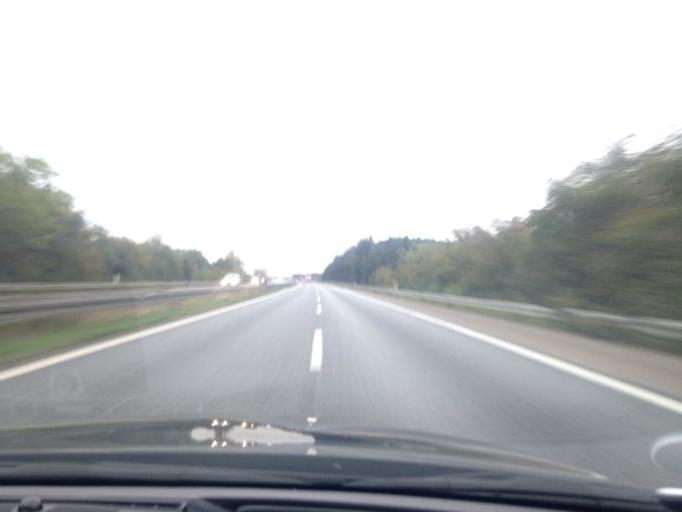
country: DK
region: South Denmark
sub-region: Haderslev Kommune
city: Haderslev
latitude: 55.2723
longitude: 9.4238
